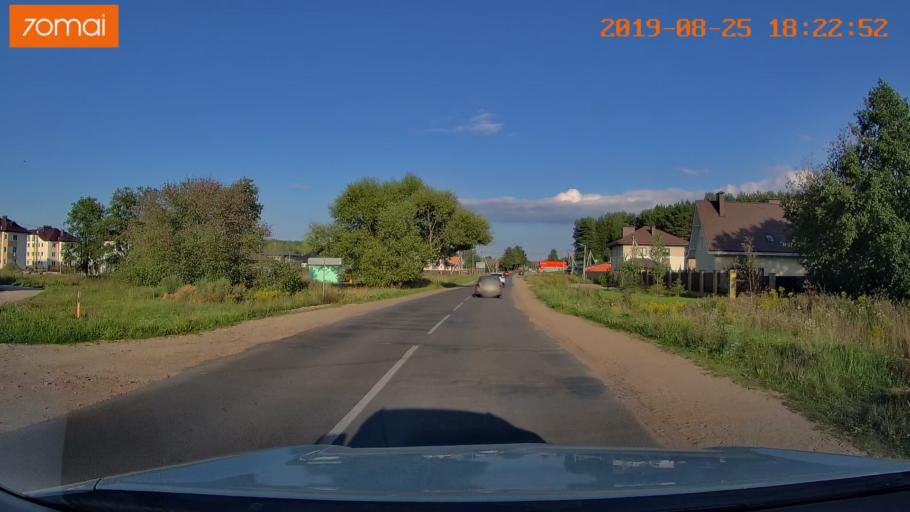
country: BY
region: Minsk
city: Khatsyezhyna
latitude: 53.9398
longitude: 27.3235
